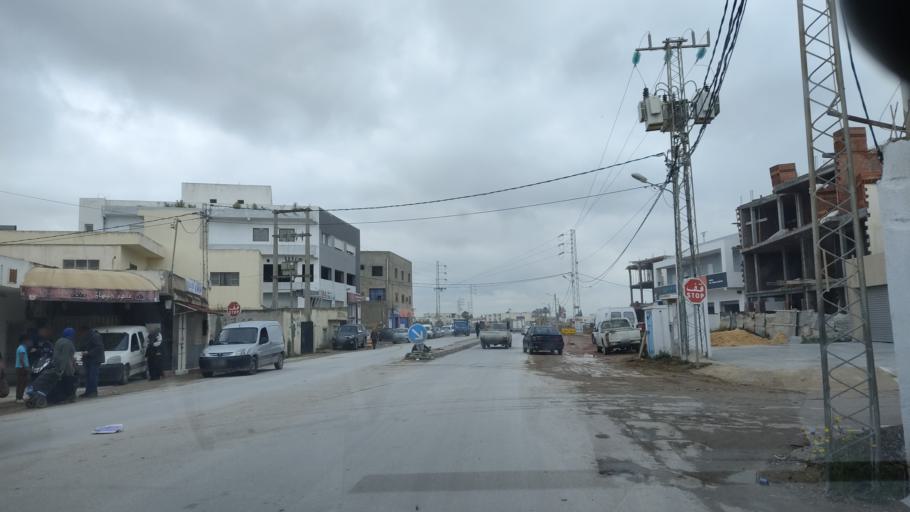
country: TN
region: Ariana
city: Ariana
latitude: 36.8902
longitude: 10.2129
